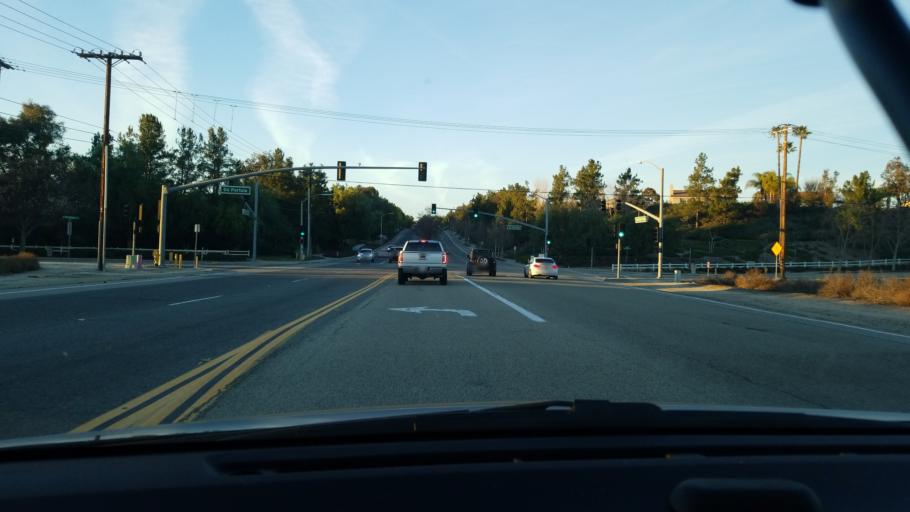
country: US
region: California
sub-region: Riverside County
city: Temecula
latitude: 33.4891
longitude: -117.0800
